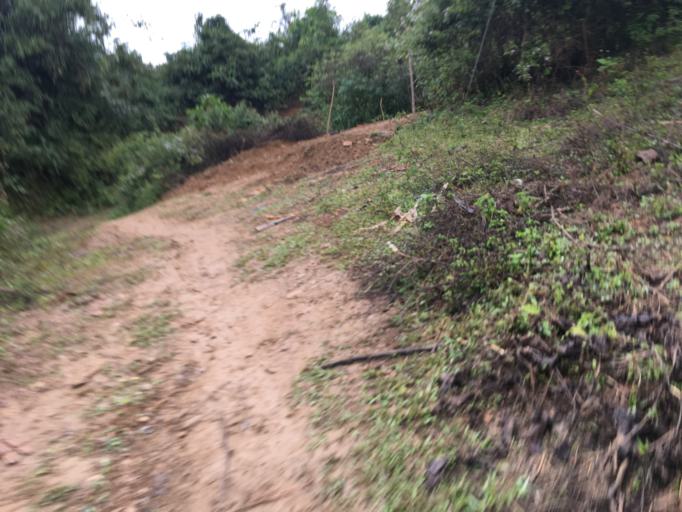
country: LA
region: Houaphan
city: Xamtay
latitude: 19.8980
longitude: 104.4602
